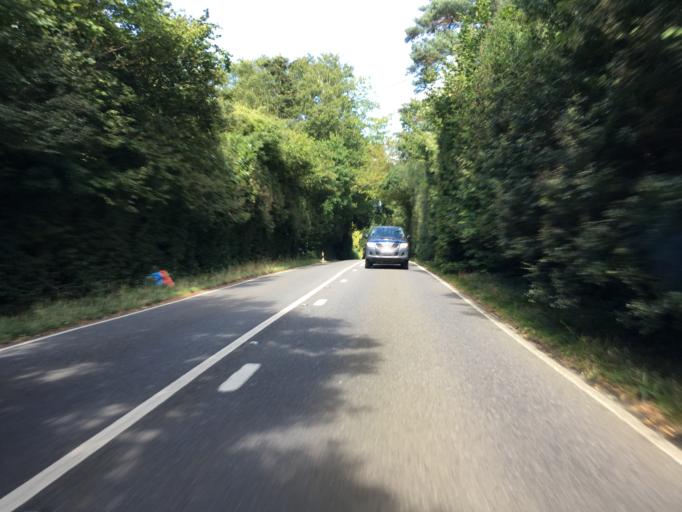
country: GB
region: England
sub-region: West Sussex
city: Southwater
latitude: 51.0537
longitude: -0.4025
